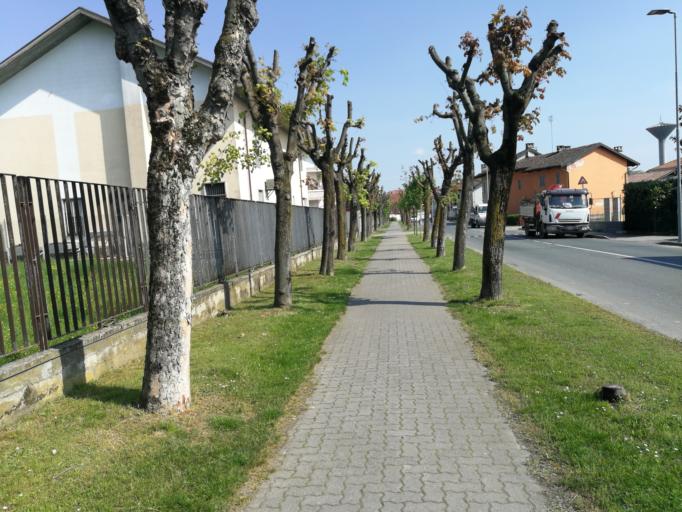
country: IT
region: Piedmont
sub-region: Provincia di Cuneo
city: Moretta
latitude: 44.7665
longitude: 7.5319
